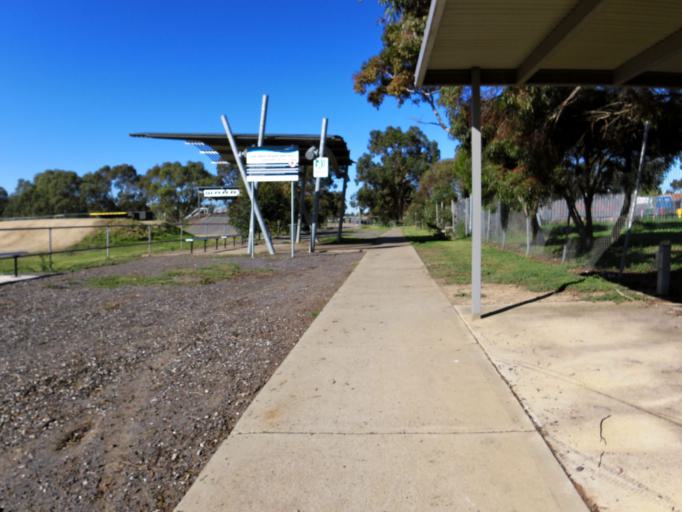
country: AU
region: Victoria
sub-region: Wyndham
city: Tarneit
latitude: -37.8832
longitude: 144.6778
